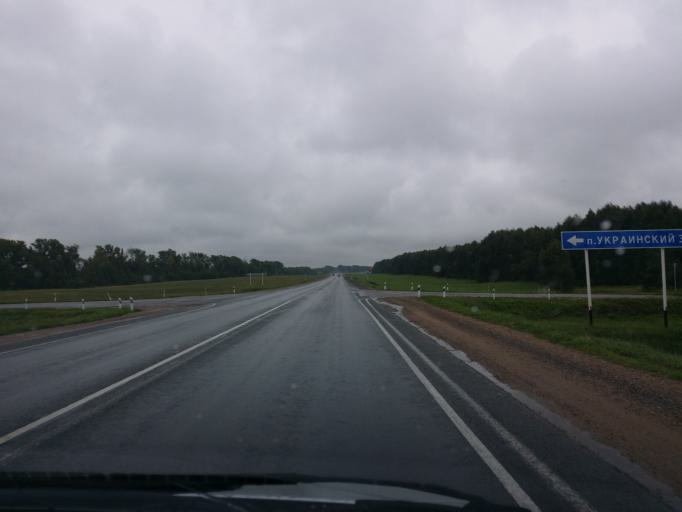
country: RU
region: Altai Krai
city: Bayunovskiye Klyuchi
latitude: 53.2930
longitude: 84.3052
